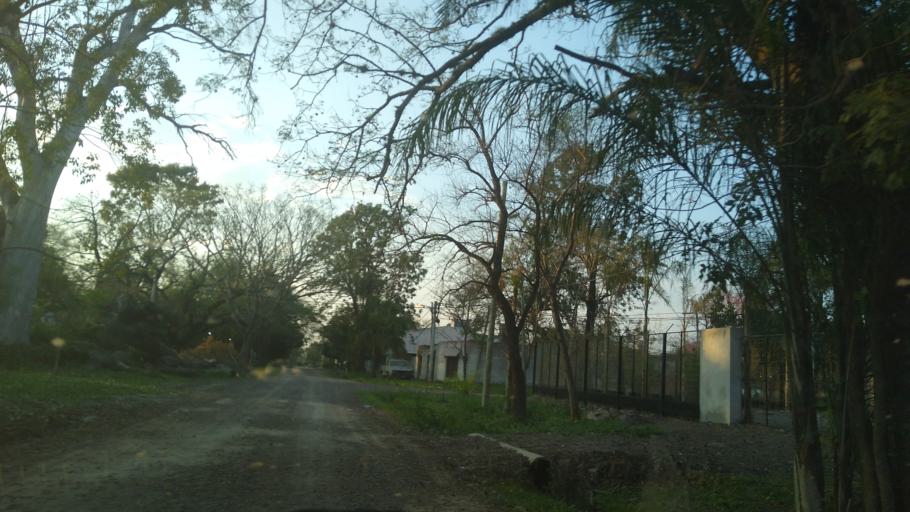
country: AR
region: Chaco
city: Barranqueras
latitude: -27.4683
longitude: -58.9566
